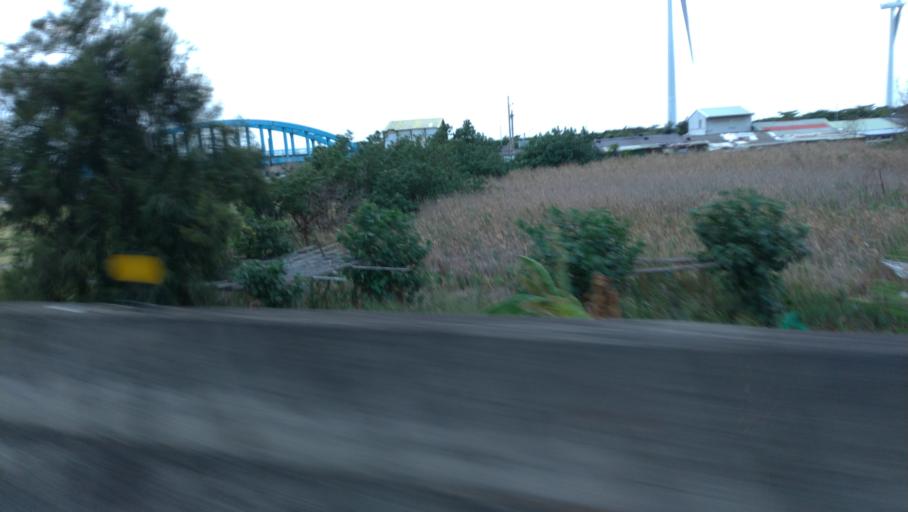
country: TW
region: Taiwan
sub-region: Hsinchu
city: Hsinchu
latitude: 24.7608
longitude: 120.9074
